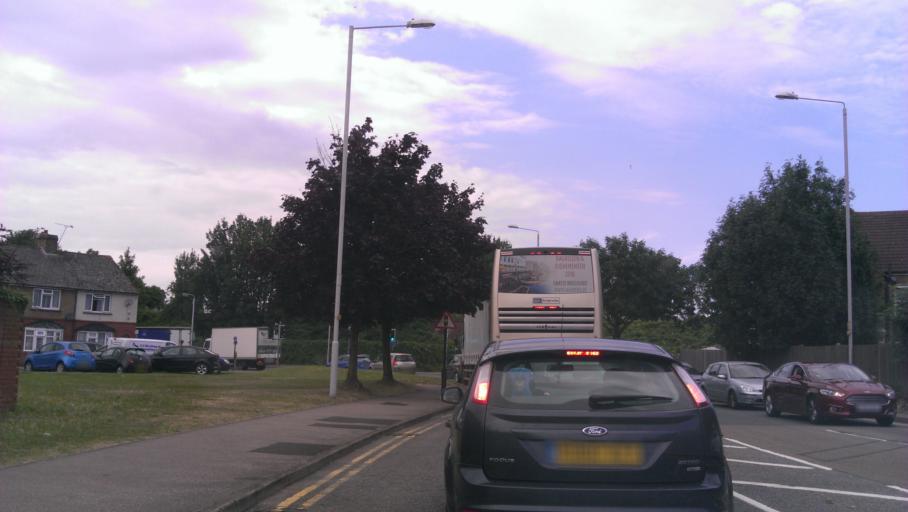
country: GB
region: England
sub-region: Kent
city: Sittingbourne
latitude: 51.3396
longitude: 0.7452
